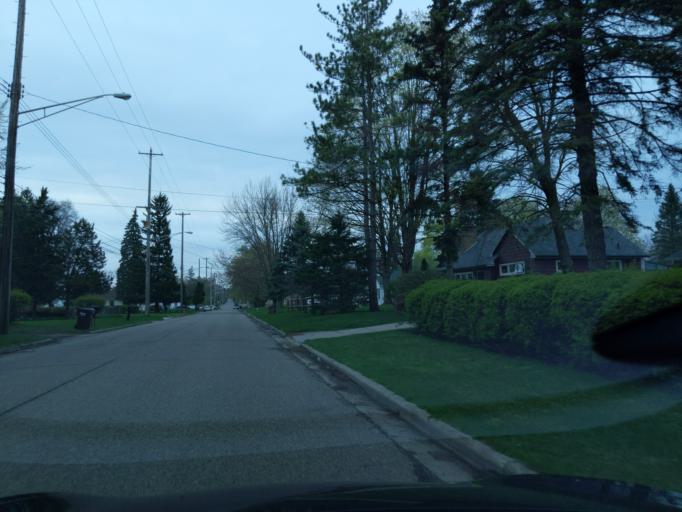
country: US
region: Michigan
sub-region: Eaton County
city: Waverly
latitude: 42.7379
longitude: -84.6090
